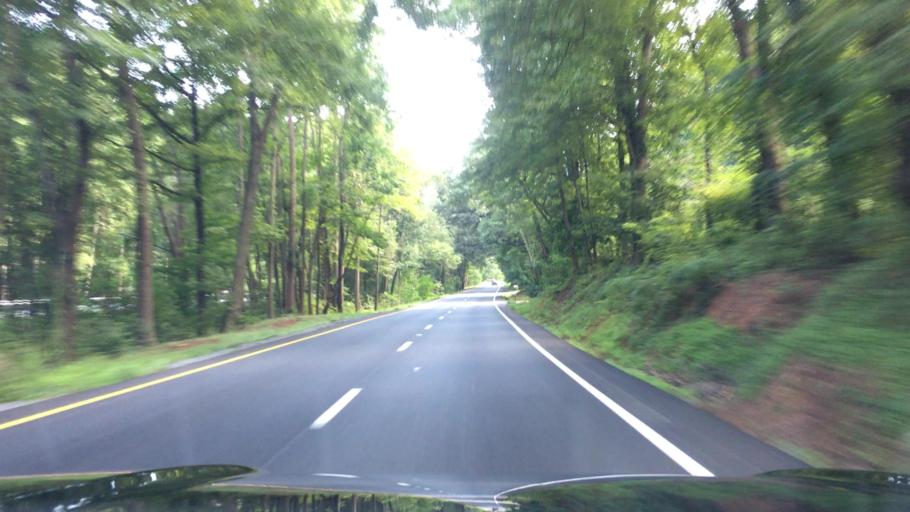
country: US
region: Virginia
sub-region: Albemarle County
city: Crozet
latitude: 37.9476
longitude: -78.6640
